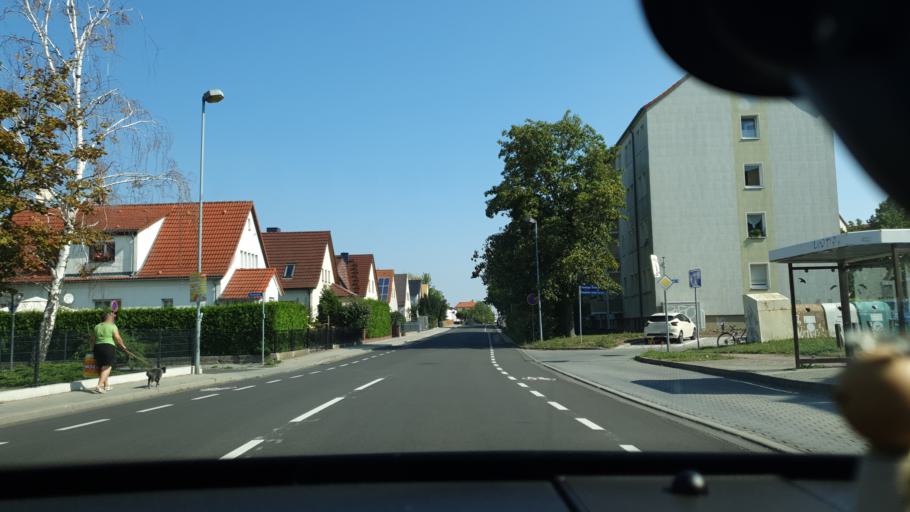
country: DE
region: Saxony
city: Torgau
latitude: 51.5551
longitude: 12.9841
